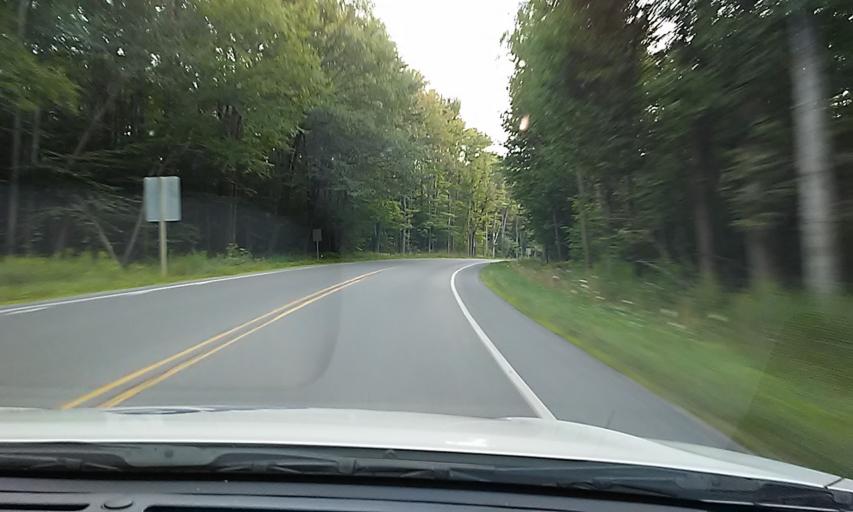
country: US
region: Pennsylvania
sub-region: McKean County
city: Kane
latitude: 41.6192
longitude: -78.8291
